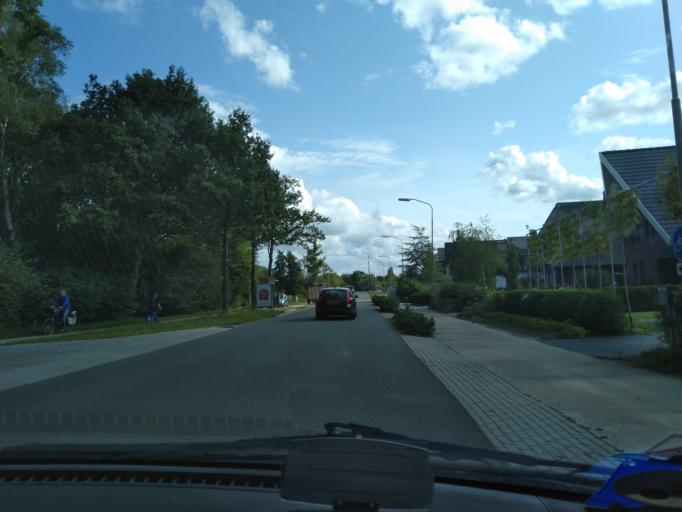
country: NL
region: Groningen
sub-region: Gemeente Groningen
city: Groningen
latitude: 53.1741
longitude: 6.5460
